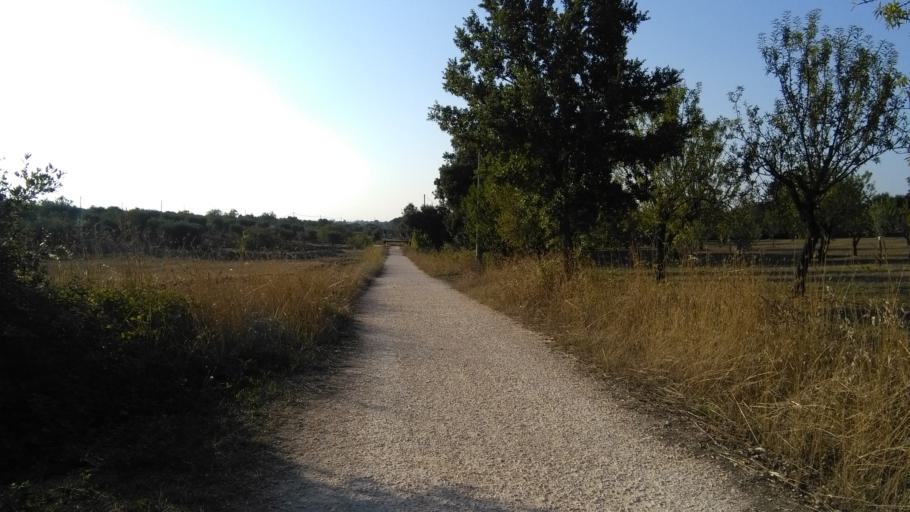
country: IT
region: Apulia
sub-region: Provincia di Brindisi
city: Cisternino
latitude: 40.7211
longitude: 17.3989
